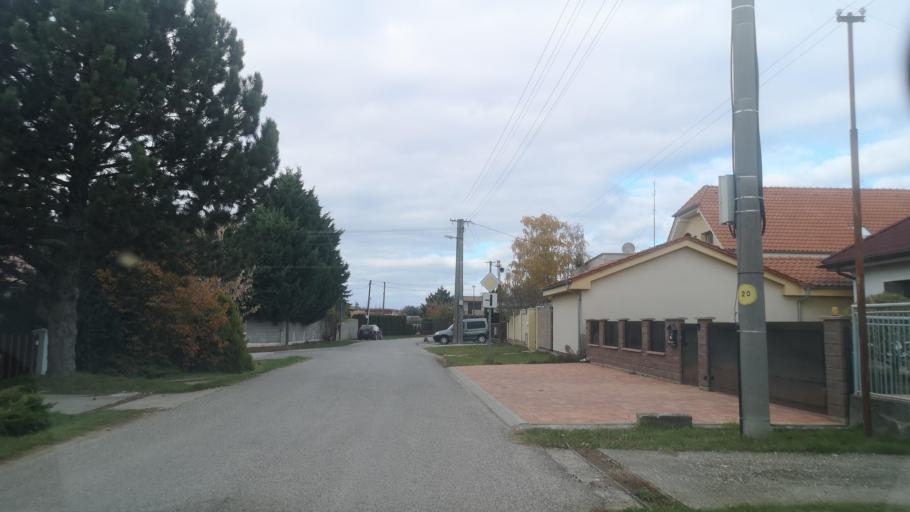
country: SK
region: Nitriansky
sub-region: Okres Nitra
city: Nitra
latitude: 48.3119
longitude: 17.9434
